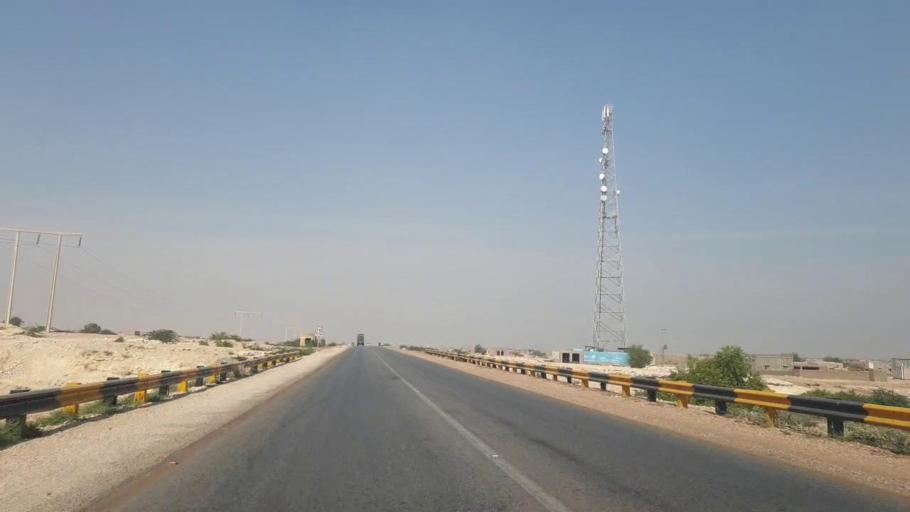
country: PK
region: Sindh
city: Hala
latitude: 25.7727
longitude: 68.2860
